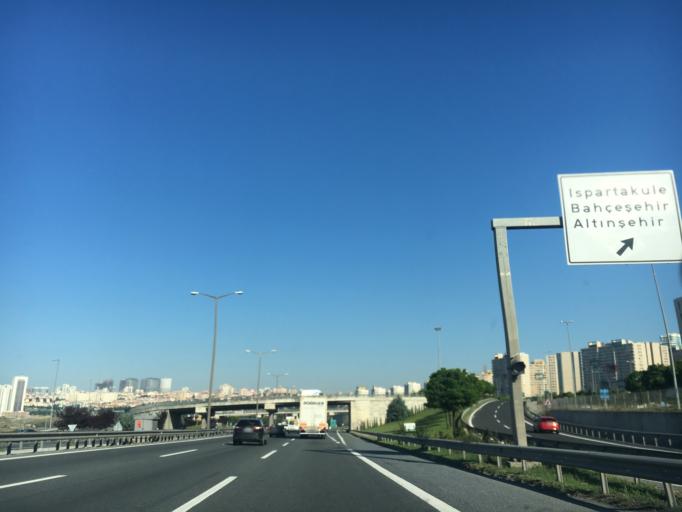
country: TR
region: Istanbul
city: Esenyurt
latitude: 41.0556
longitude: 28.7143
